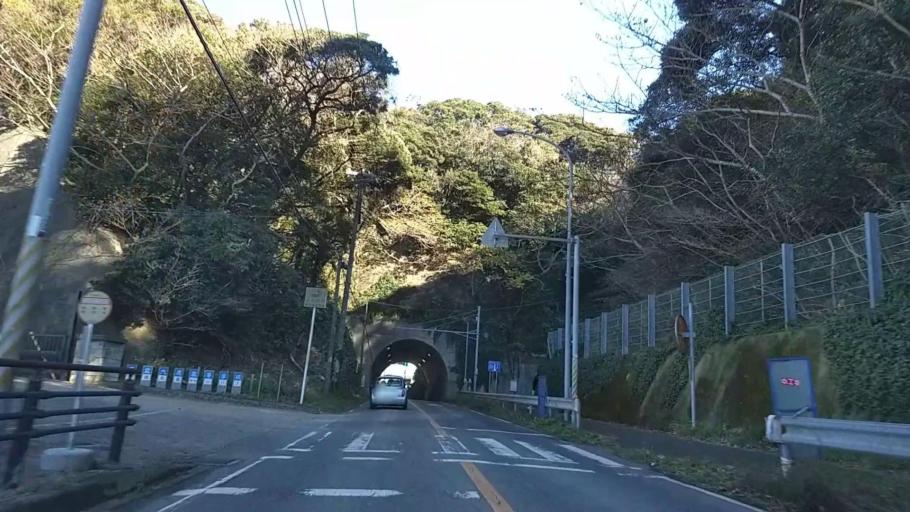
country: JP
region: Chiba
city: Katsuura
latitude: 35.1546
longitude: 140.3212
